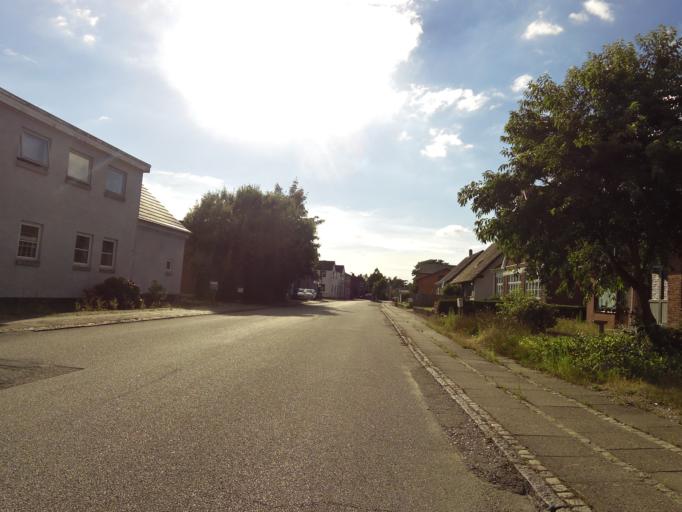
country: DK
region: South Denmark
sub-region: Haderslev Kommune
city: Vojens
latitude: 55.1970
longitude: 9.3002
